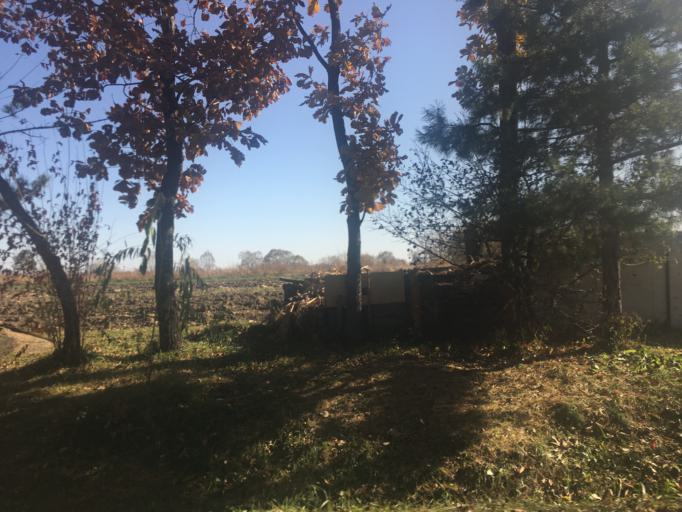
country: RU
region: Primorskiy
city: Dal'nerechensk
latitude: 45.8851
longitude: 133.7418
